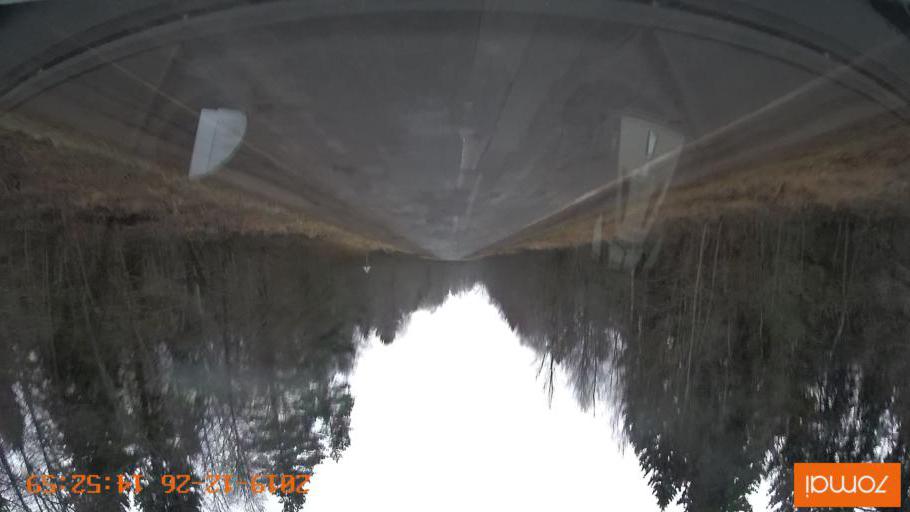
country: RU
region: Jaroslavl
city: Rybinsk
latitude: 58.3182
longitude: 38.8932
